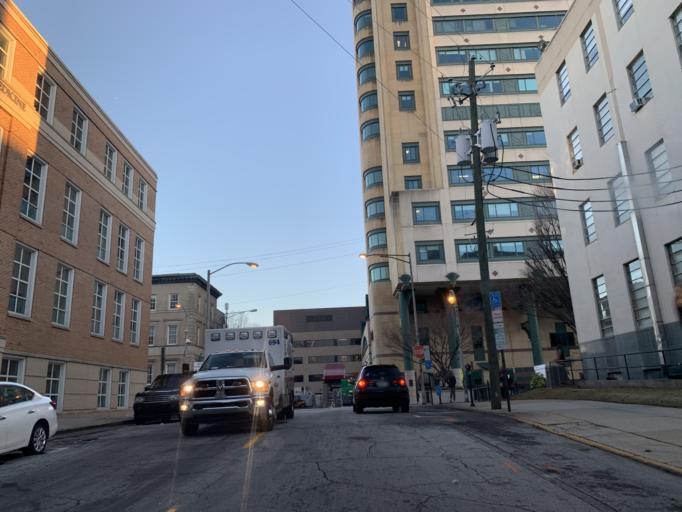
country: US
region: Georgia
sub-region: Fulton County
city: Atlanta
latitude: 33.7530
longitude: -84.3824
